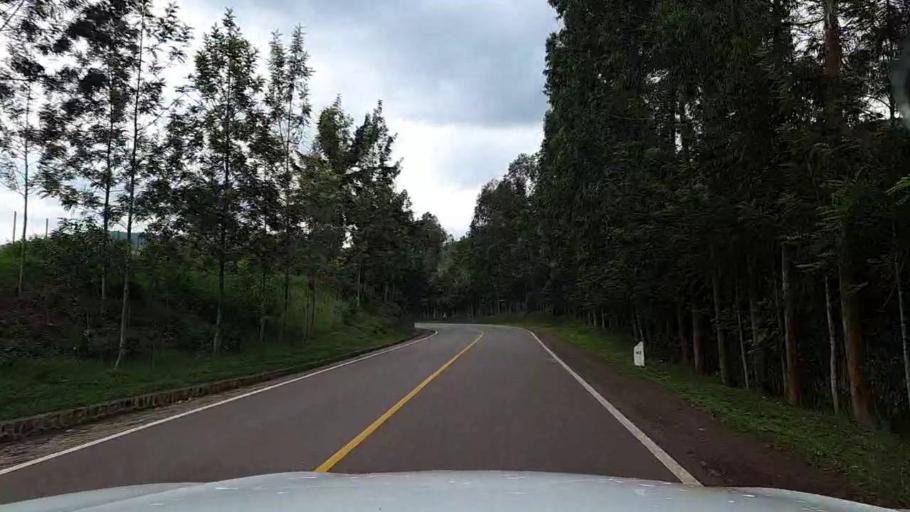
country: RW
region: Northern Province
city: Byumba
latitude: -1.6828
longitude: 30.1042
